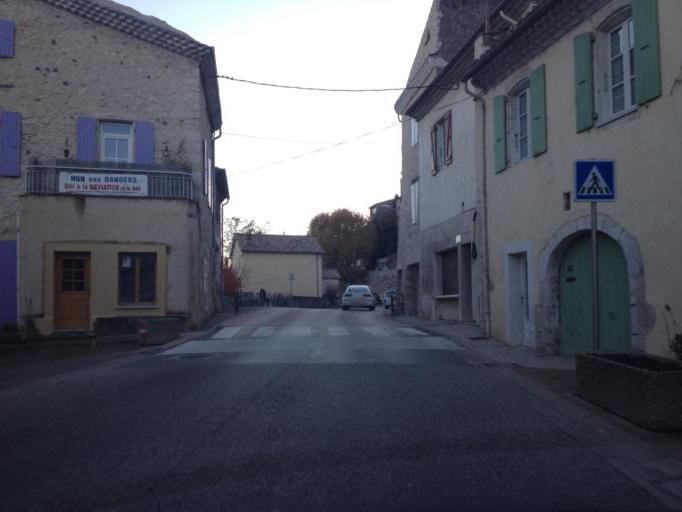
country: FR
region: Rhone-Alpes
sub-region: Departement de l'Ardeche
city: Rochemaure
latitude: 44.5878
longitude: 4.7043
